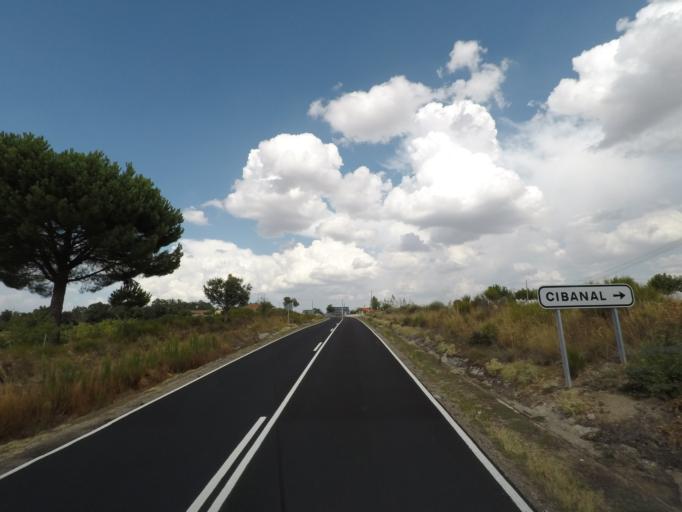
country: ES
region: Castille and Leon
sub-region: Provincia de Zamora
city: Fermoselle
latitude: 41.3139
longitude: -6.3078
